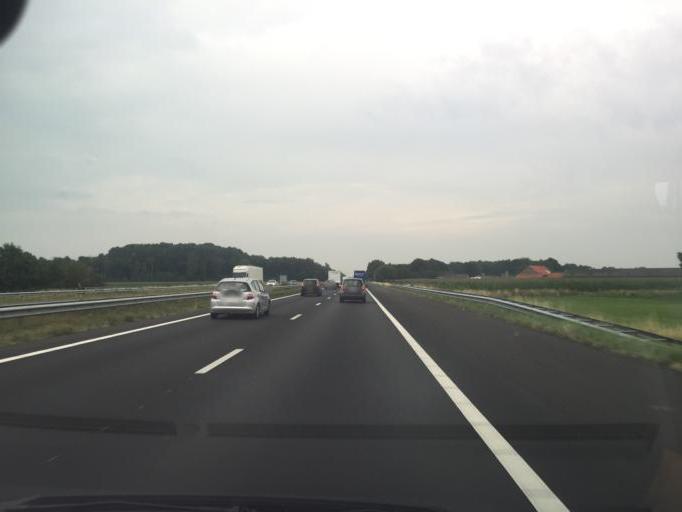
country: NL
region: North Brabant
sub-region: Gemeente Asten
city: Asten
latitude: 51.3996
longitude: 5.8306
